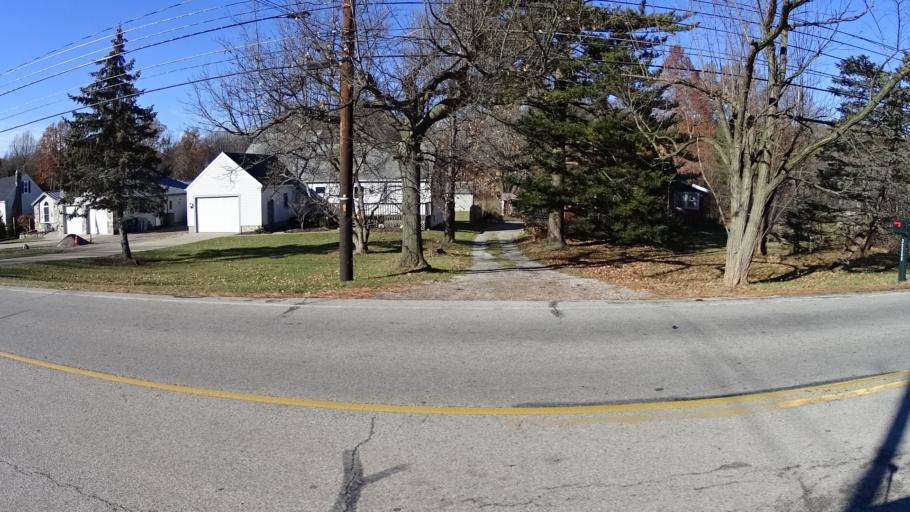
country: US
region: Ohio
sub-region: Lorain County
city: North Ridgeville
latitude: 41.4114
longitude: -81.9749
